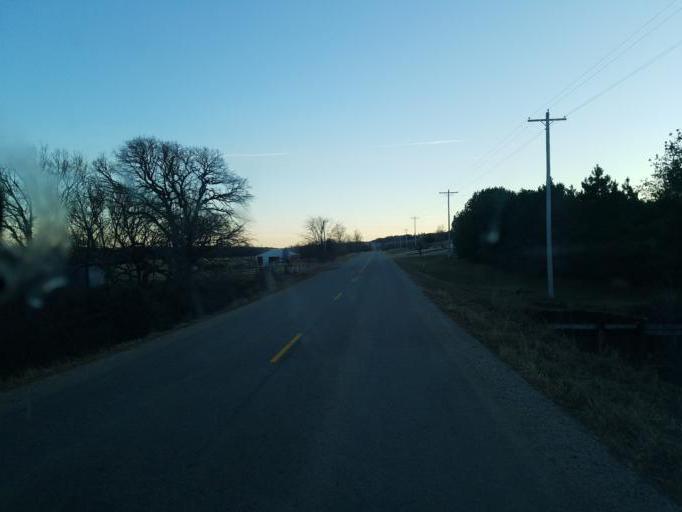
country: US
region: Nebraska
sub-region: Knox County
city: Center
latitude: 42.6559
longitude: -97.8873
